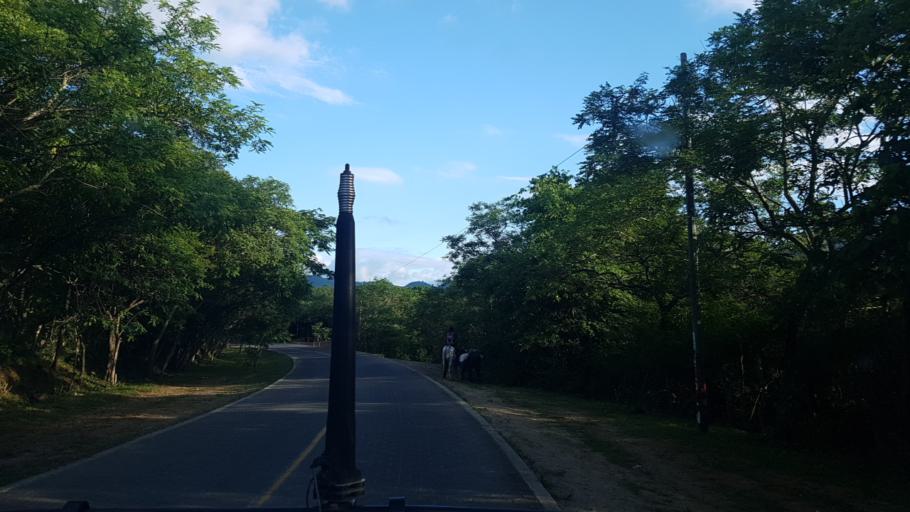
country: NI
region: Nueva Segovia
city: Ocotal
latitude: 13.6443
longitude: -86.6028
